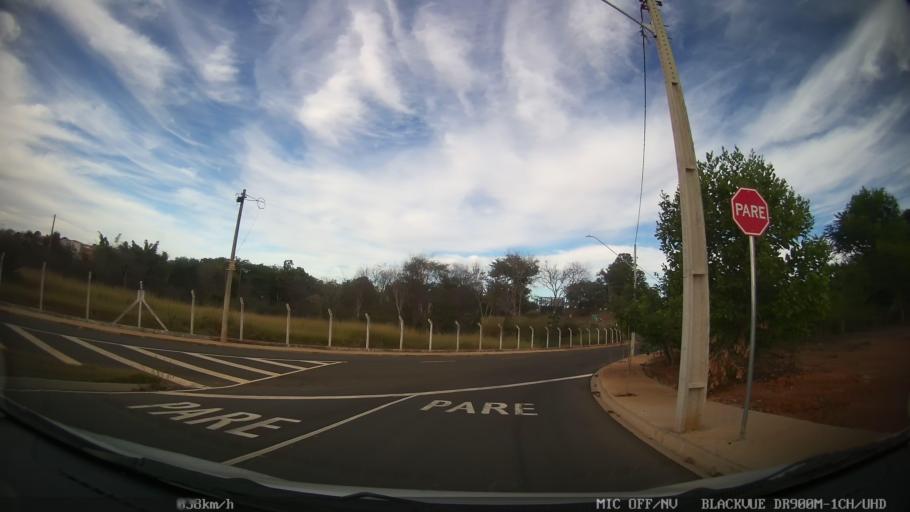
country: BR
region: Sao Paulo
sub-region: Catanduva
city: Catanduva
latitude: -21.1420
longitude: -49.0075
